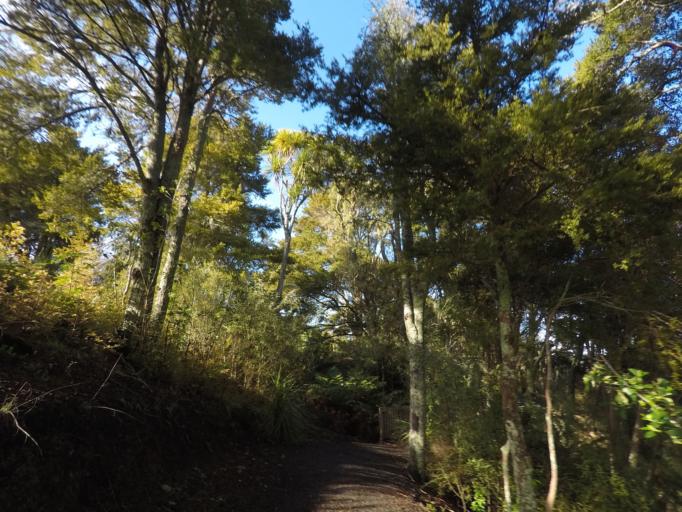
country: NZ
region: Auckland
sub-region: Auckland
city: Warkworth
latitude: -36.4285
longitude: 174.7184
